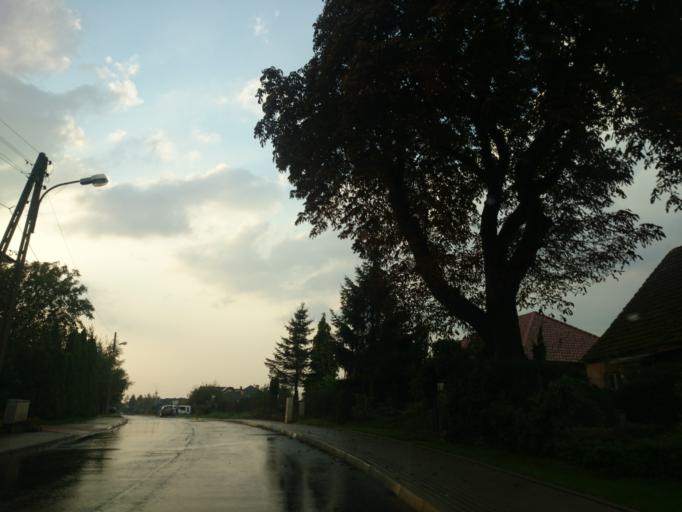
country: PL
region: West Pomeranian Voivodeship
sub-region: Powiat policki
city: Przeclaw
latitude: 53.3856
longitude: 14.4606
